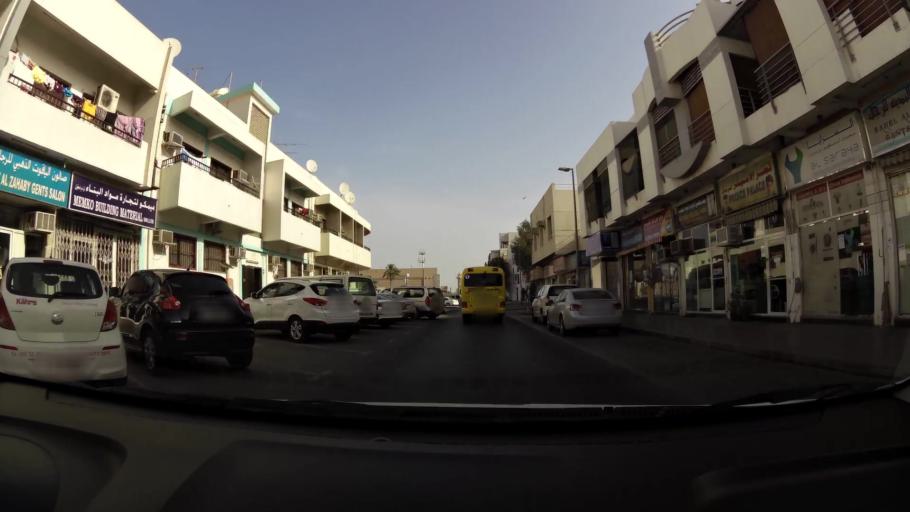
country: AE
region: Ash Shariqah
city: Sharjah
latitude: 25.2802
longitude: 55.3342
